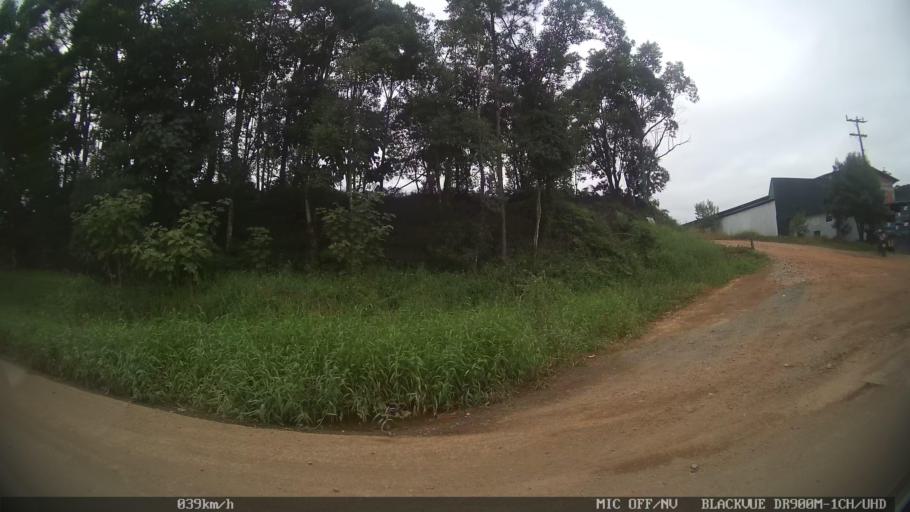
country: BR
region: Santa Catarina
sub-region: Joinville
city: Joinville
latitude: -26.2585
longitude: -48.8833
